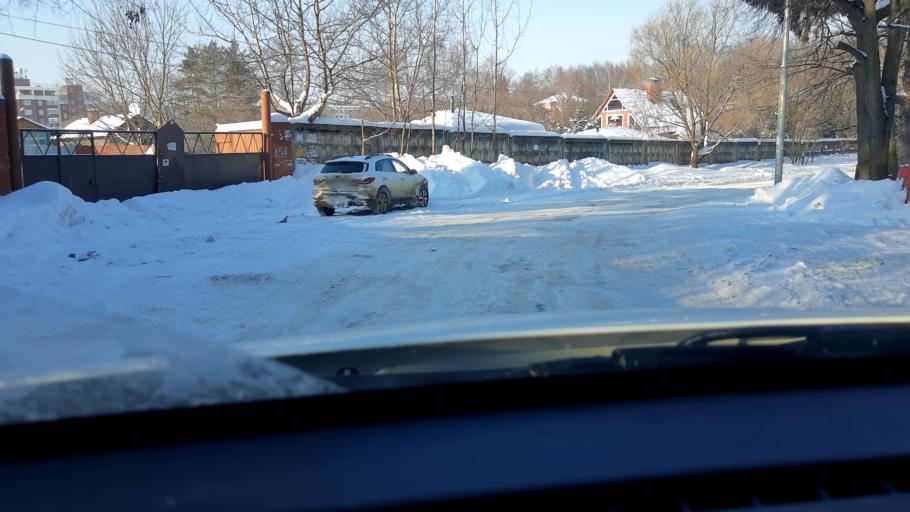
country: RU
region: Moskovskaya
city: Troitsk
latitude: 55.4988
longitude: 37.3117
